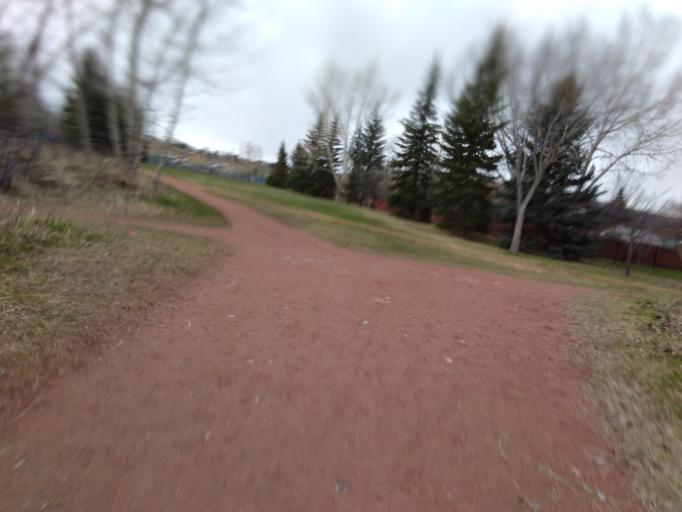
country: CA
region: Alberta
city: Cochrane
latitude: 51.1865
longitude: -114.4812
